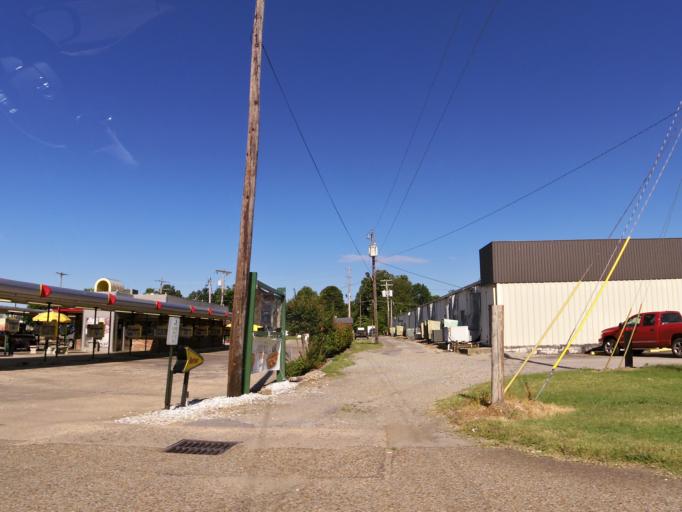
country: US
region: Arkansas
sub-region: Clay County
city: Corning
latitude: 36.4136
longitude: -90.5865
